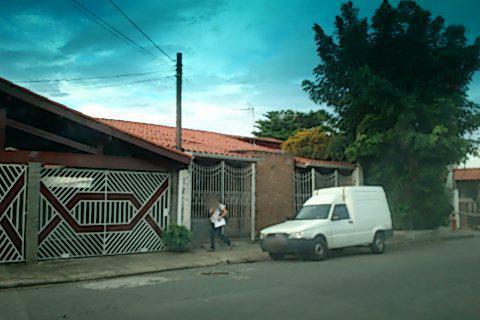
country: BR
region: Sao Paulo
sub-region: Sao Jose Dos Campos
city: Sao Jose dos Campos
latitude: -23.1858
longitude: -45.8742
